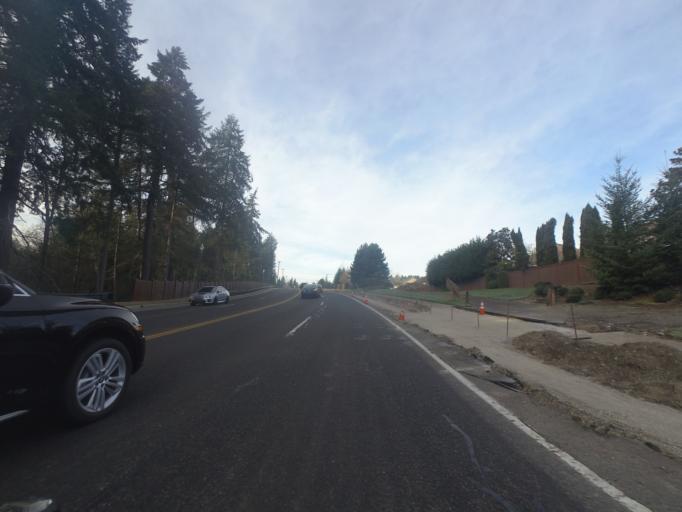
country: US
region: Washington
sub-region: Pierce County
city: Lakewood
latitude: 47.1988
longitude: -122.5240
